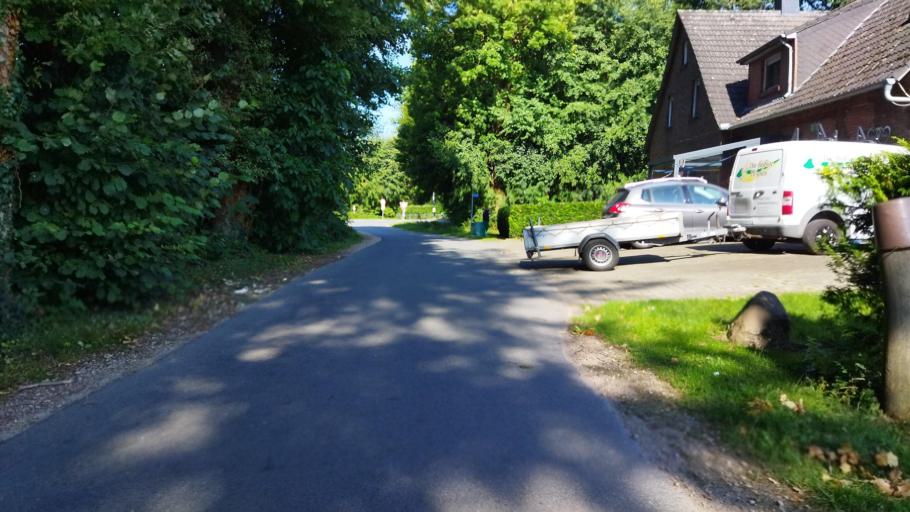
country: DE
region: North Rhine-Westphalia
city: Lengerich
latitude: 52.1593
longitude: 7.8973
